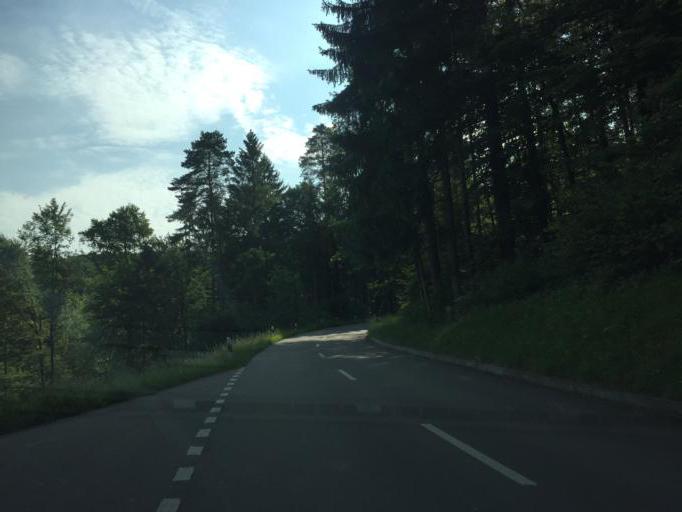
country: CH
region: Zurich
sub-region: Bezirk Buelach
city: Rorbas
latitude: 47.5597
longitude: 8.5679
